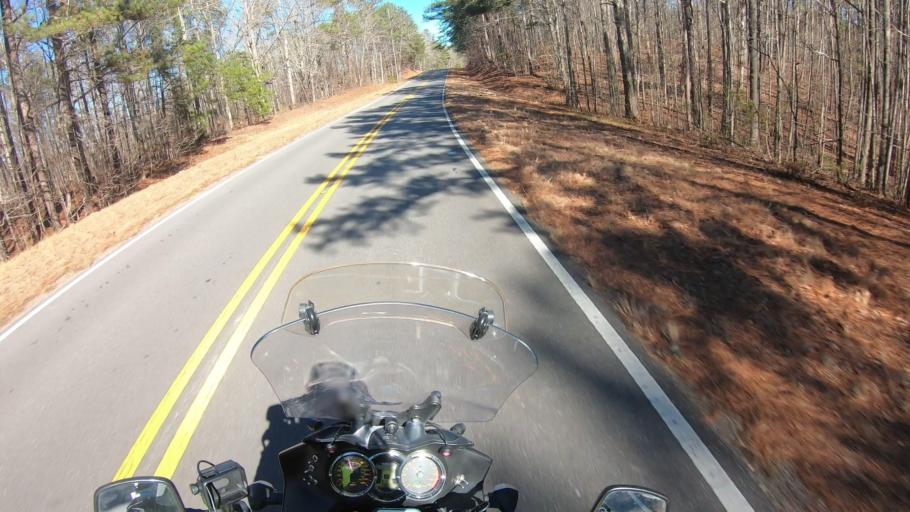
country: US
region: Alabama
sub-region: Calhoun County
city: Choccolocco
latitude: 33.5698
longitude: -85.6984
